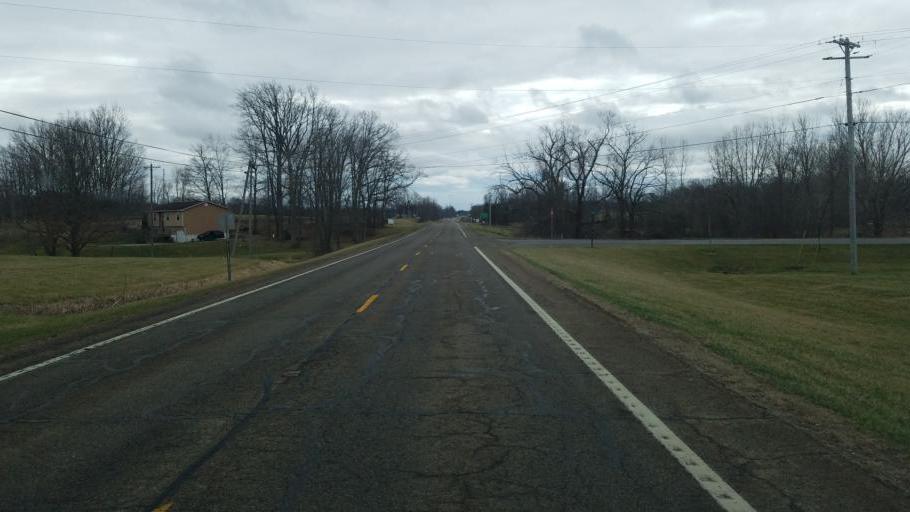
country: US
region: Ohio
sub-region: Morrow County
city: Mount Gilead
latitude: 40.5155
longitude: -82.7443
